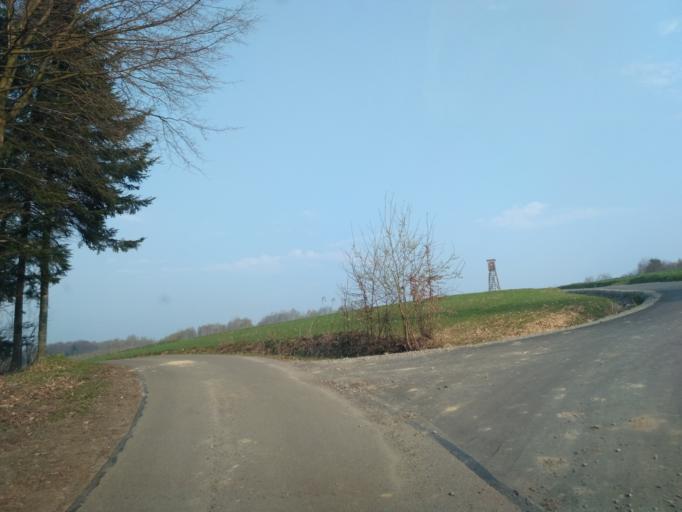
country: PL
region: Subcarpathian Voivodeship
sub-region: Powiat strzyzowski
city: Wisniowa
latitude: 49.8855
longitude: 21.6336
